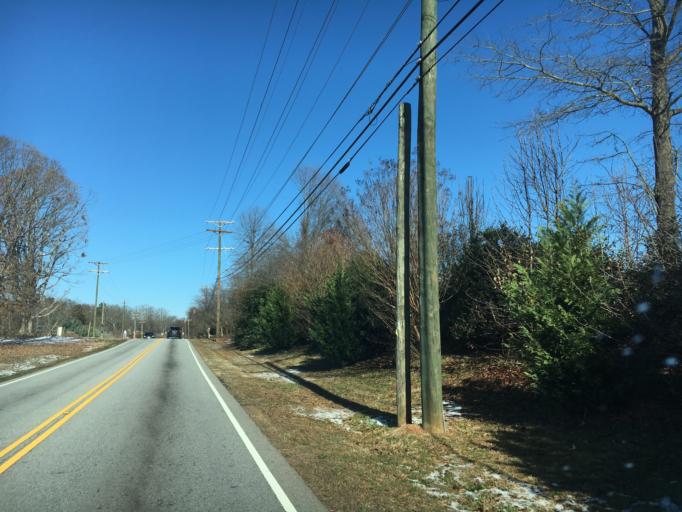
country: US
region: South Carolina
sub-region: Greenville County
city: Taylors
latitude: 34.9271
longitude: -82.2686
